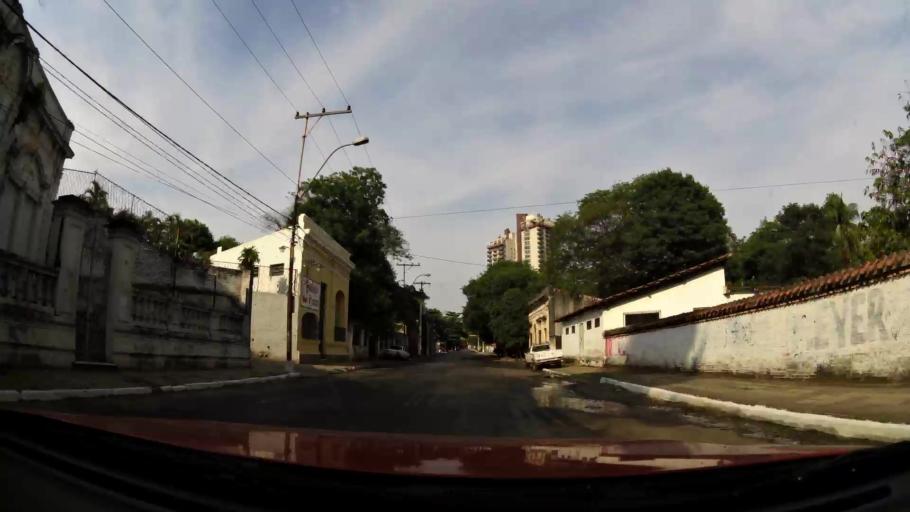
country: PY
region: Asuncion
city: Asuncion
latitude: -25.2831
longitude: -57.6201
